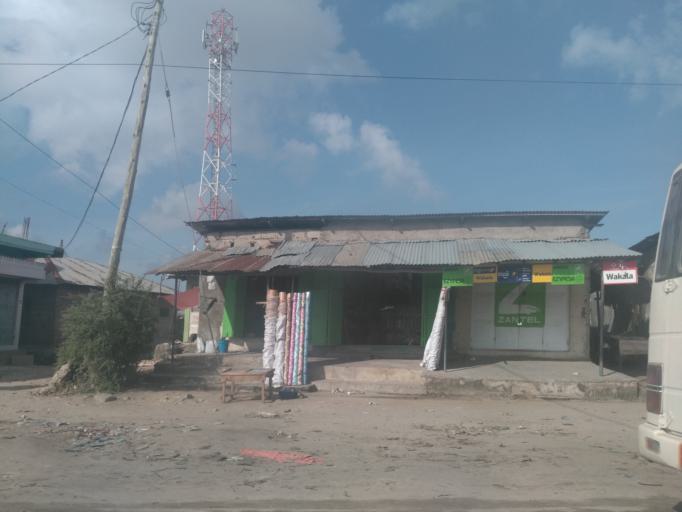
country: TZ
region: Zanzibar Urban/West
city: Zanzibar
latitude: -6.1560
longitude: 39.2235
